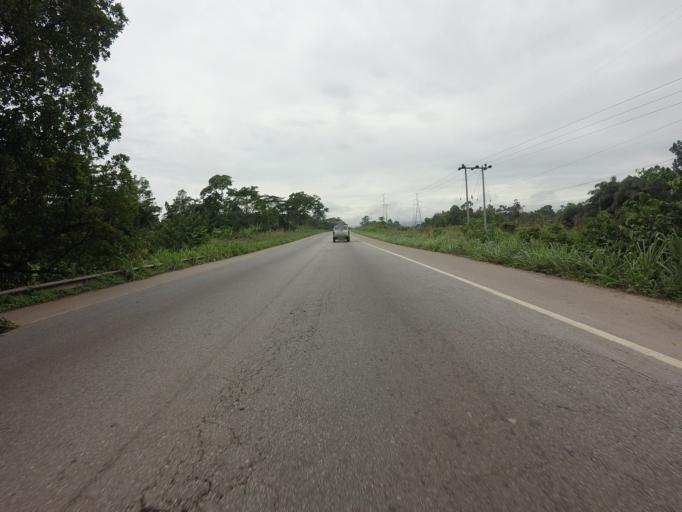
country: GH
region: Eastern
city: Begoro
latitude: 6.4116
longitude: -0.5698
